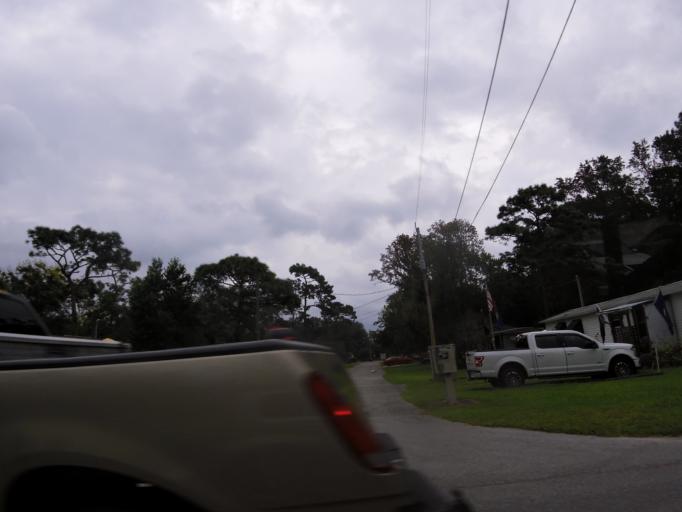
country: US
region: Florida
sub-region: Clay County
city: Bellair-Meadowbrook Terrace
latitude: 30.2287
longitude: -81.7729
